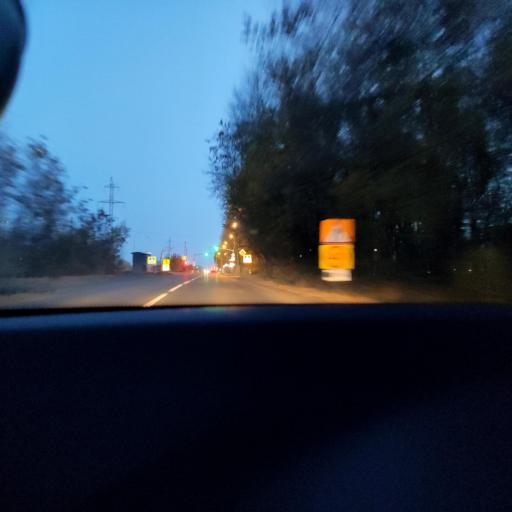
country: RU
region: Samara
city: Petra-Dubrava
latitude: 53.3092
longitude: 50.2768
